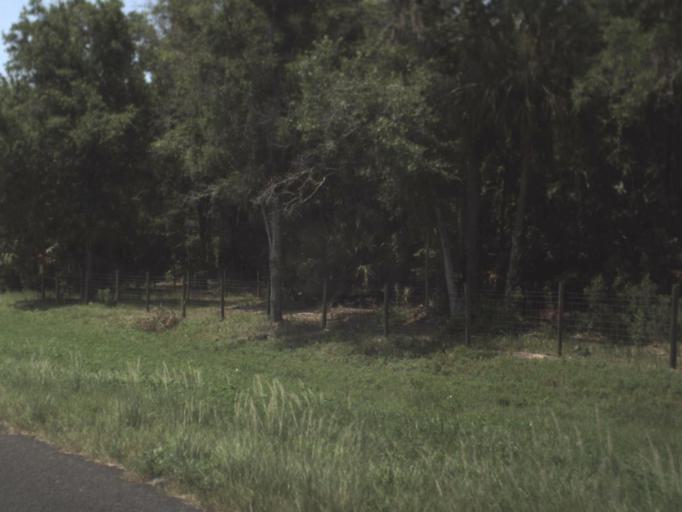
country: US
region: Florida
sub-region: Levy County
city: Inglis
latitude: 29.0187
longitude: -82.6676
